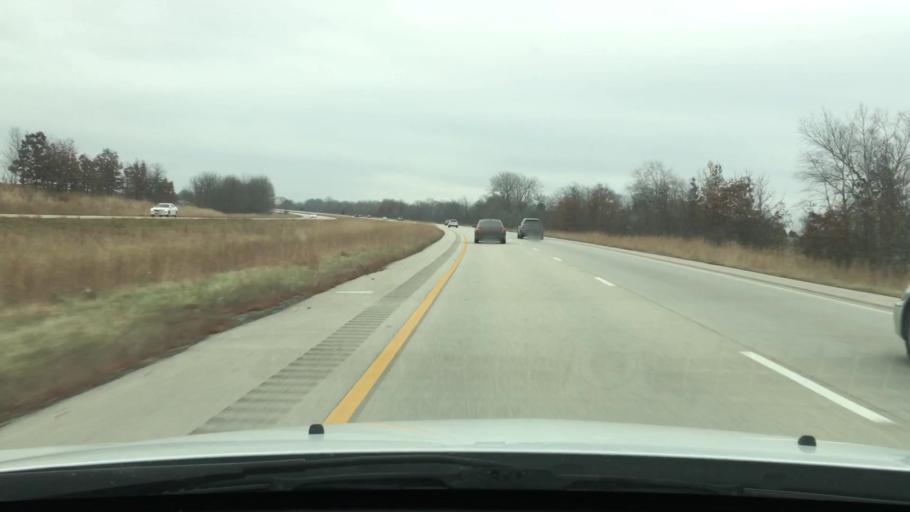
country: US
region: Illinois
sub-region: Sangamon County
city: New Berlin
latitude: 39.7413
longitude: -89.8290
